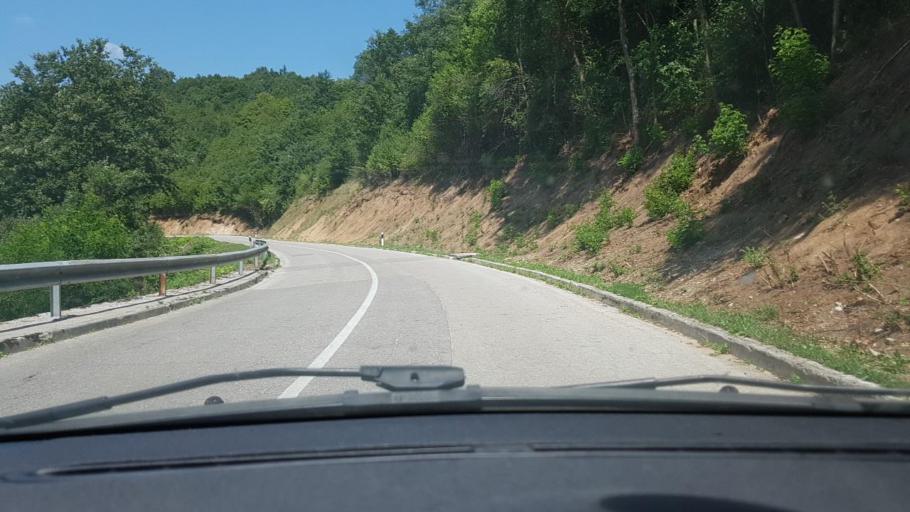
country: BA
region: Federation of Bosnia and Herzegovina
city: Orasac
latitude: 44.5724
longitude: 16.0826
